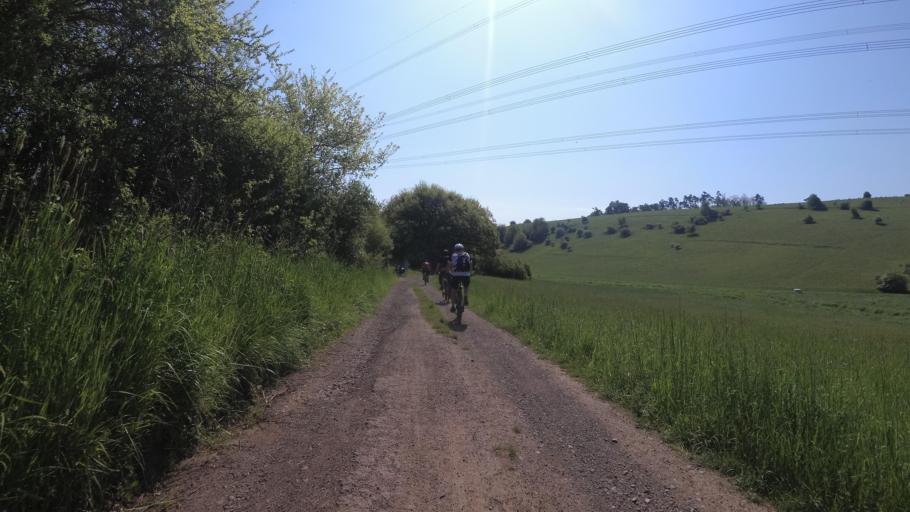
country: DE
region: Rheinland-Pfalz
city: Gries
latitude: 49.4249
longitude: 7.4189
